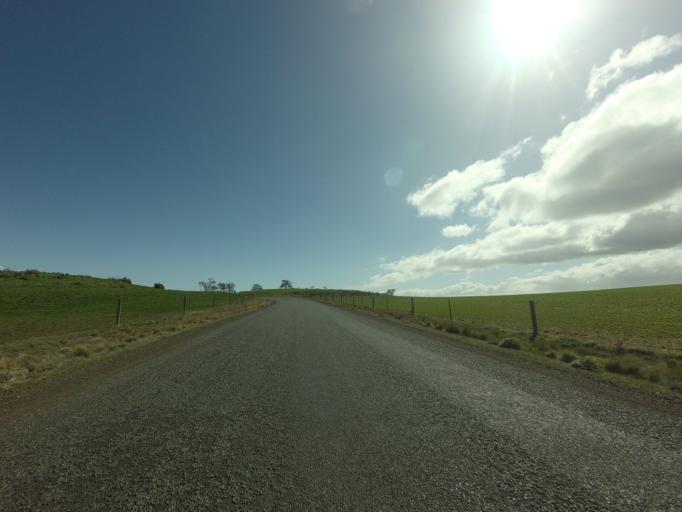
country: AU
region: Tasmania
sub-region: Northern Midlands
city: Evandale
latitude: -41.9113
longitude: 147.4649
